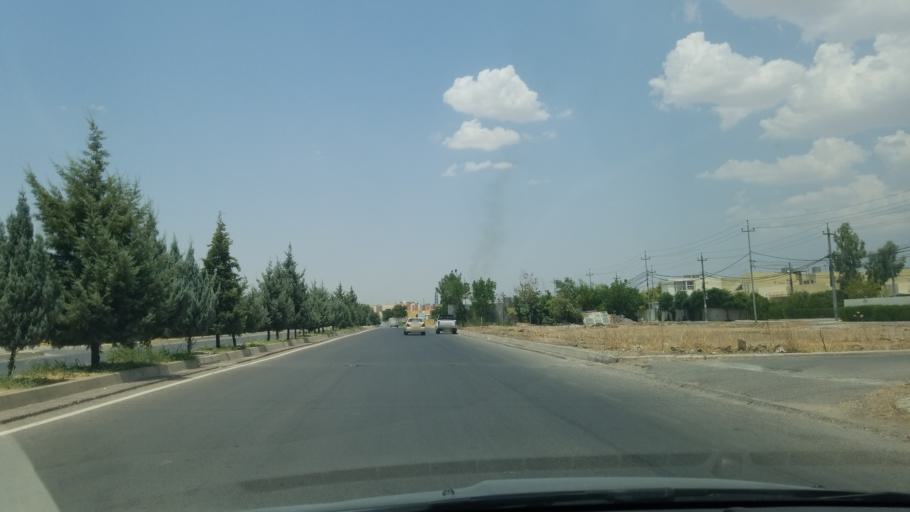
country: IQ
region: Arbil
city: Erbil
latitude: 36.1686
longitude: 44.0590
